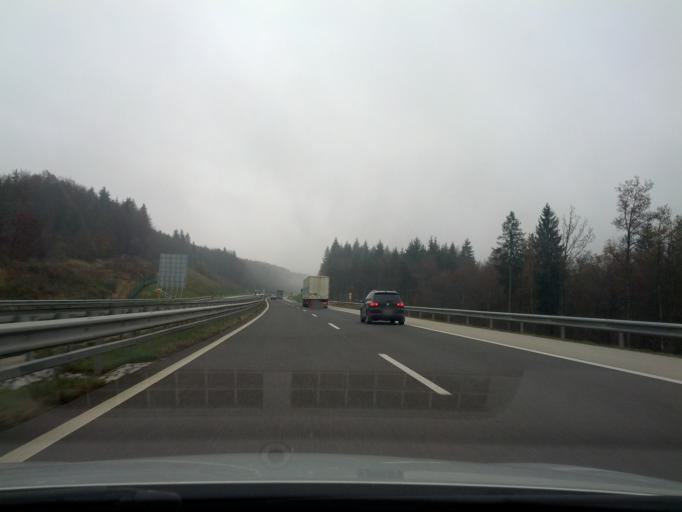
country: SI
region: Mirna Pec
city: Mirna Pec
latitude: 45.8887
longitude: 15.0641
